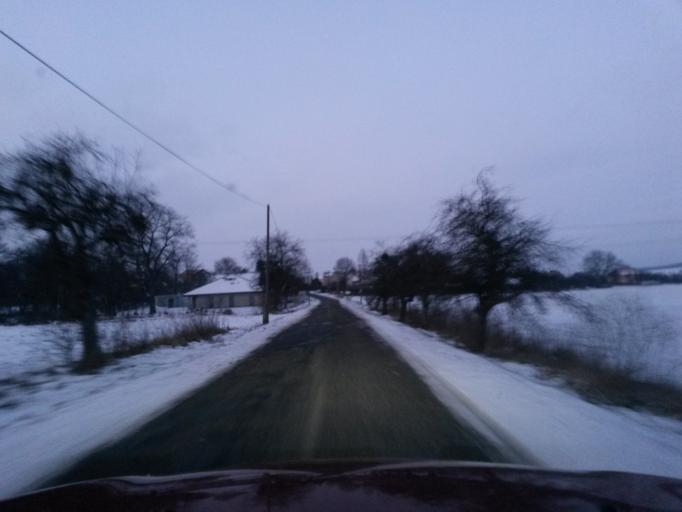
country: SK
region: Kosicky
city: Kosice
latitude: 48.7444
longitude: 21.3230
